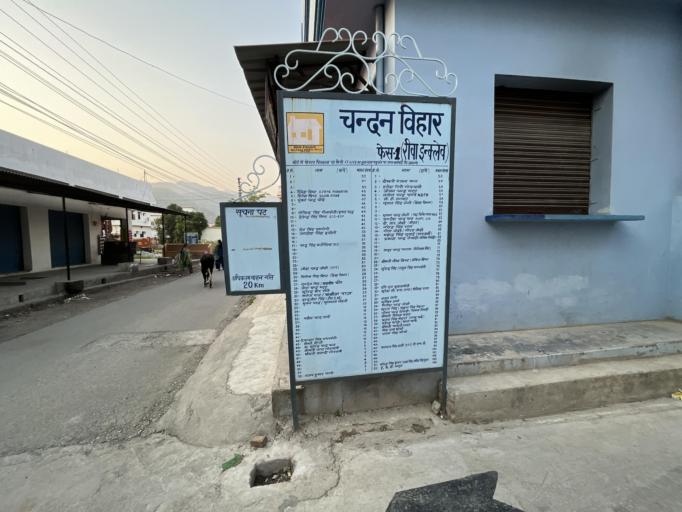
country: IN
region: Uttarakhand
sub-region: Naini Tal
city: Haldwani
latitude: 29.2308
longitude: 79.5110
